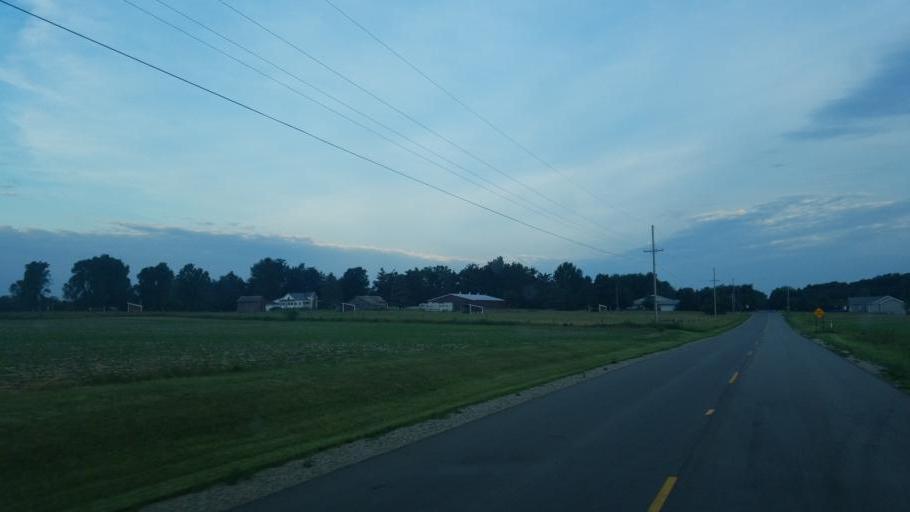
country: US
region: Michigan
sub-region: Eaton County
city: Charlotte
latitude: 42.5971
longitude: -84.8524
